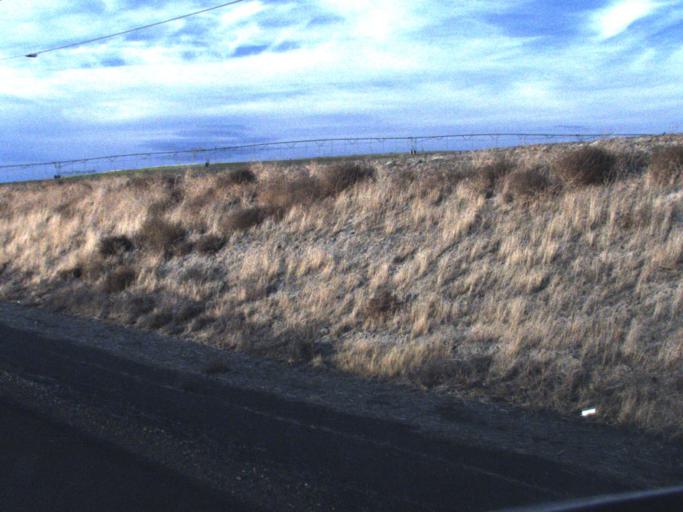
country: US
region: Washington
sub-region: Walla Walla County
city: Burbank
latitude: 46.0601
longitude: -118.7352
